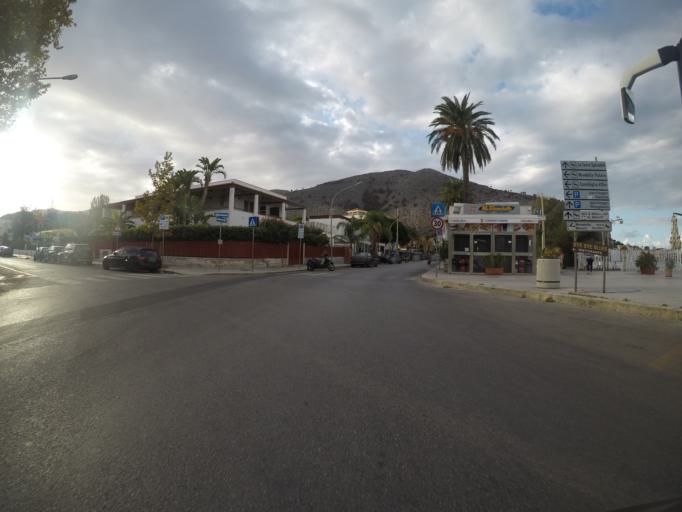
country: IT
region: Sicily
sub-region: Palermo
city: Palermo
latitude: 38.2030
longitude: 13.3259
